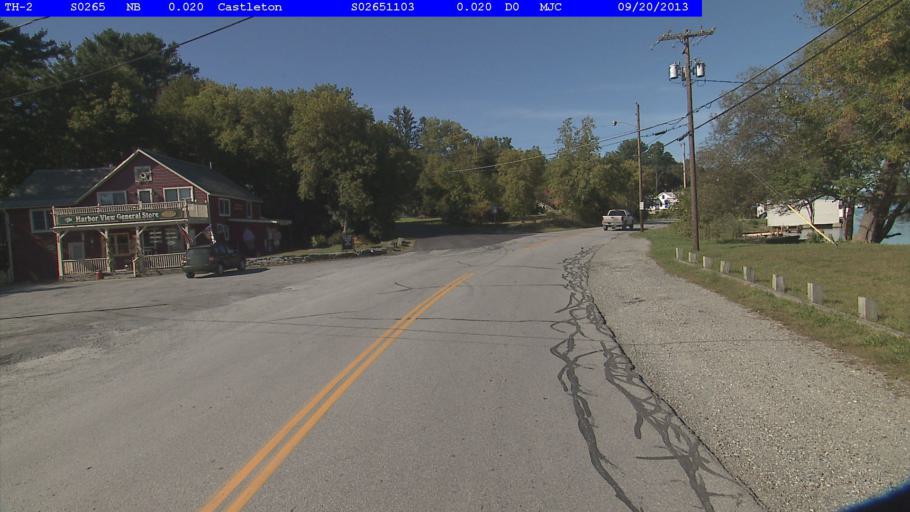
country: US
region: Vermont
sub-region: Rutland County
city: Fair Haven
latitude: 43.6050
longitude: -73.2336
